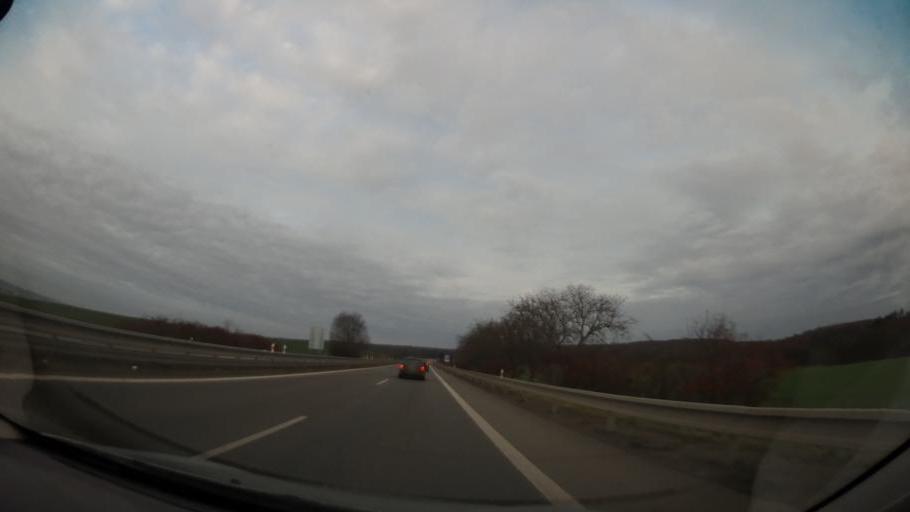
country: CZ
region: South Moravian
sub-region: Okres Brno-Venkov
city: Rosice
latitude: 49.1890
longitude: 16.4146
